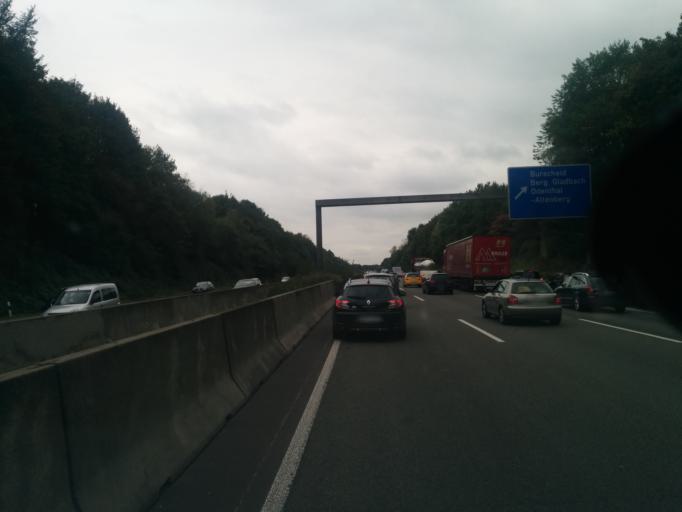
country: DE
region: North Rhine-Westphalia
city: Burscheid
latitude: 51.0885
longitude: 7.1345
